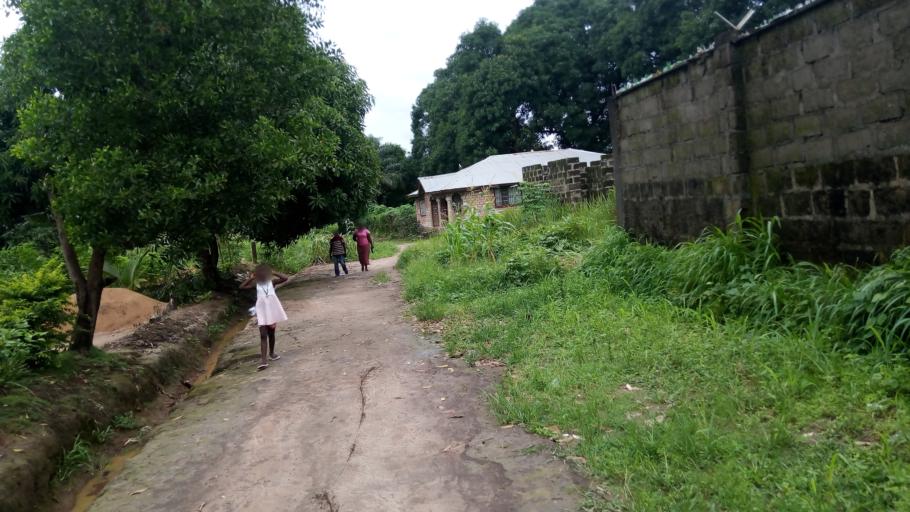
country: SL
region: Northern Province
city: Lunsar
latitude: 8.6917
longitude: -12.5336
